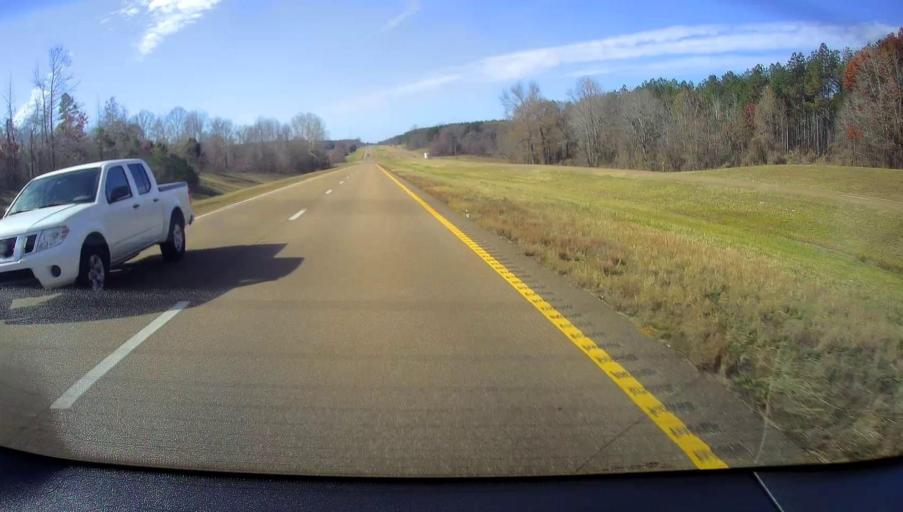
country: US
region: Mississippi
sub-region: Benton County
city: Ashland
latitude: 34.9488
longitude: -89.1003
